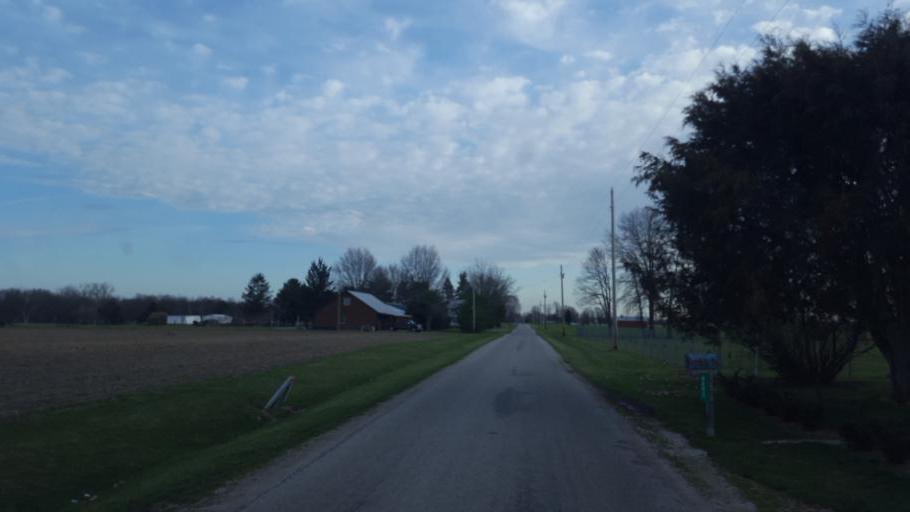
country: US
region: Ohio
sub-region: Crawford County
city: Bucyrus
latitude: 40.6783
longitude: -82.9484
